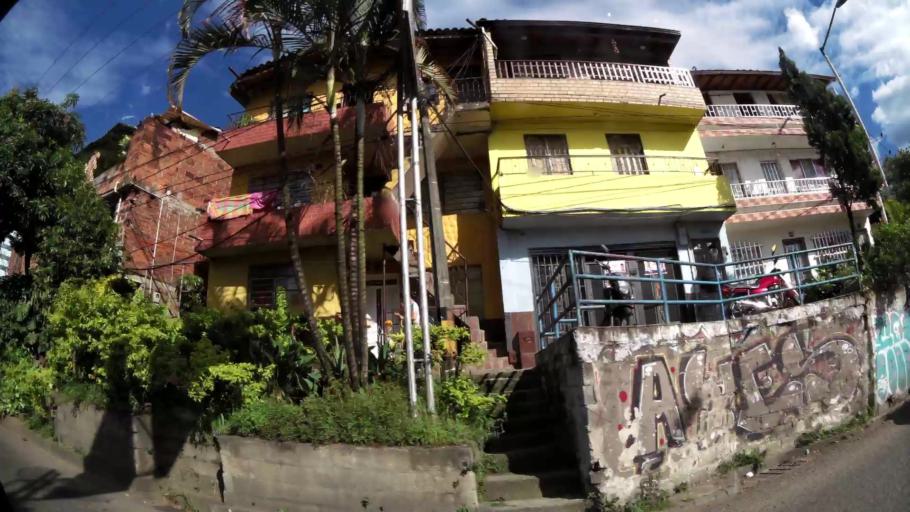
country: CO
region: Antioquia
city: Sabaneta
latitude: 6.1621
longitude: -75.6034
